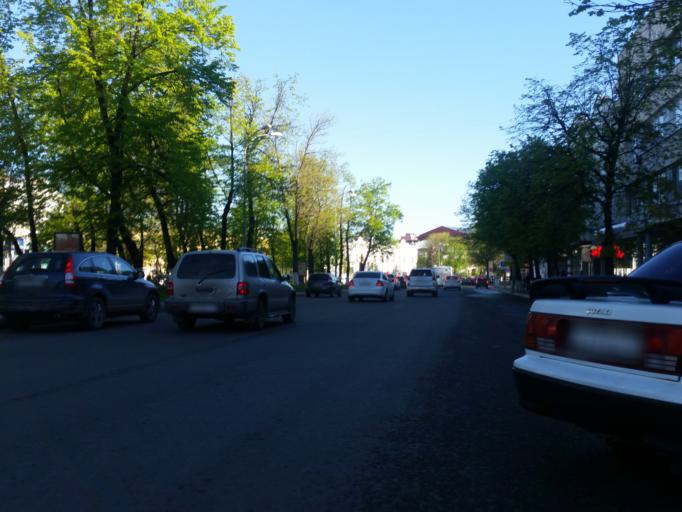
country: RU
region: Ulyanovsk
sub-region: Ulyanovskiy Rayon
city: Ulyanovsk
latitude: 54.3148
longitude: 48.3960
